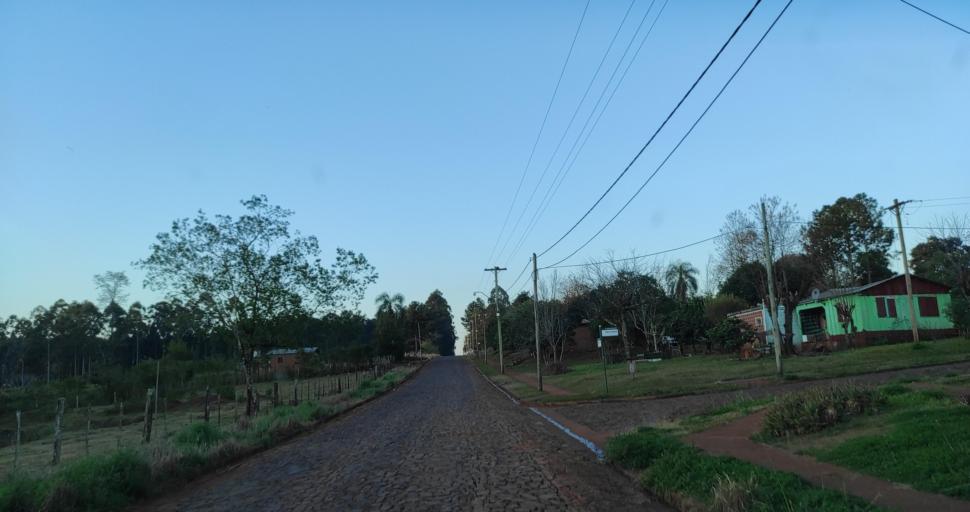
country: AR
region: Misiones
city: Capiovi
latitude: -26.8911
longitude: -55.0734
